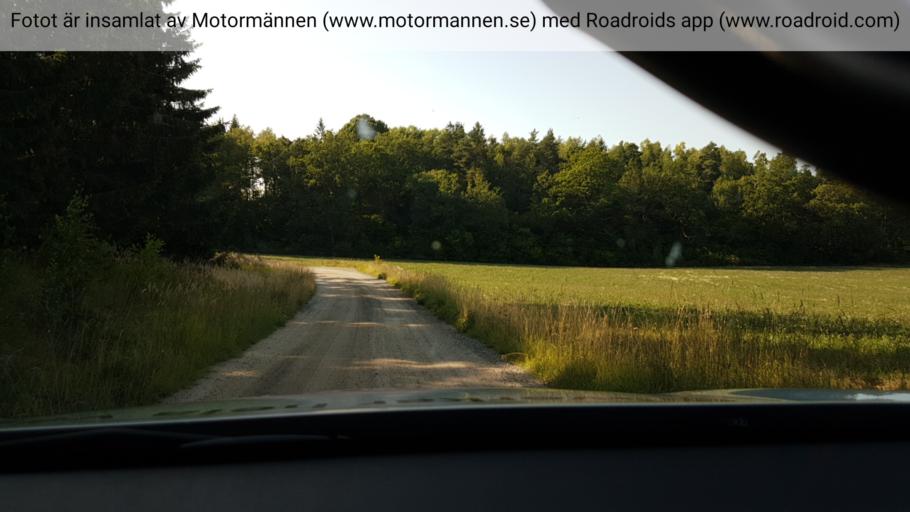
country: SE
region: Stockholm
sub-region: Nynashamns Kommun
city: Nynashamn
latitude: 58.9357
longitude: 17.9152
